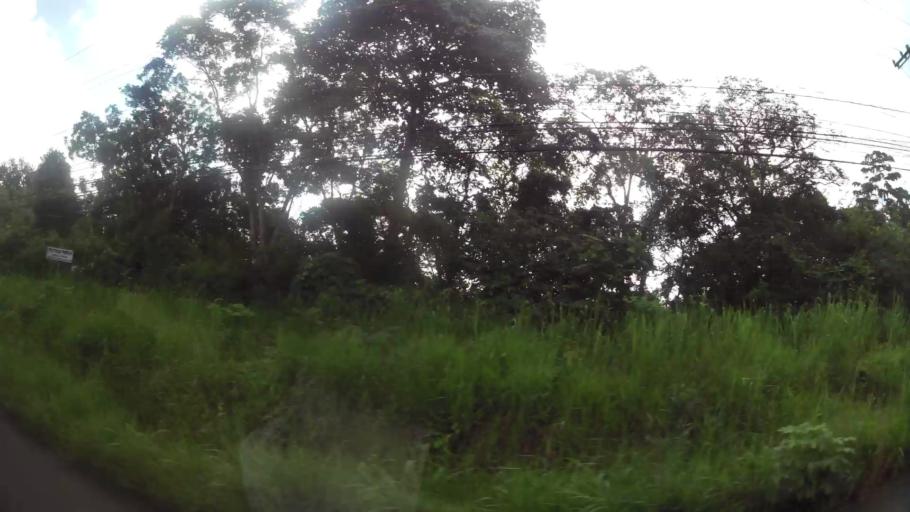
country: PA
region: Panama
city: Nuevo Arraijan
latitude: 8.9047
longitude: -79.7506
